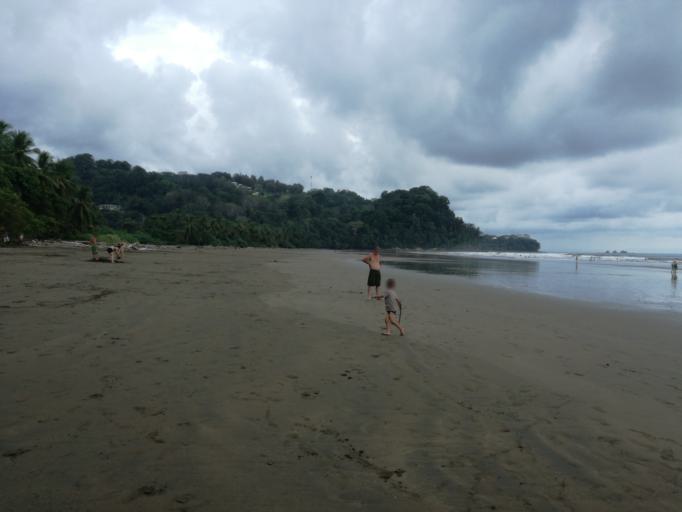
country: CR
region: San Jose
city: Mercedes
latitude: 9.1487
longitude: -83.7332
